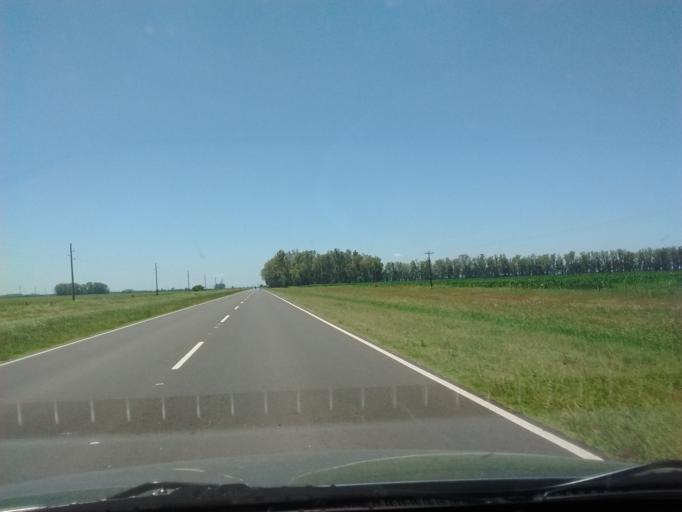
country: AR
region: Entre Rios
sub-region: Departamento de Gualeguay
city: Gualeguay
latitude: -33.0012
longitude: -59.5092
